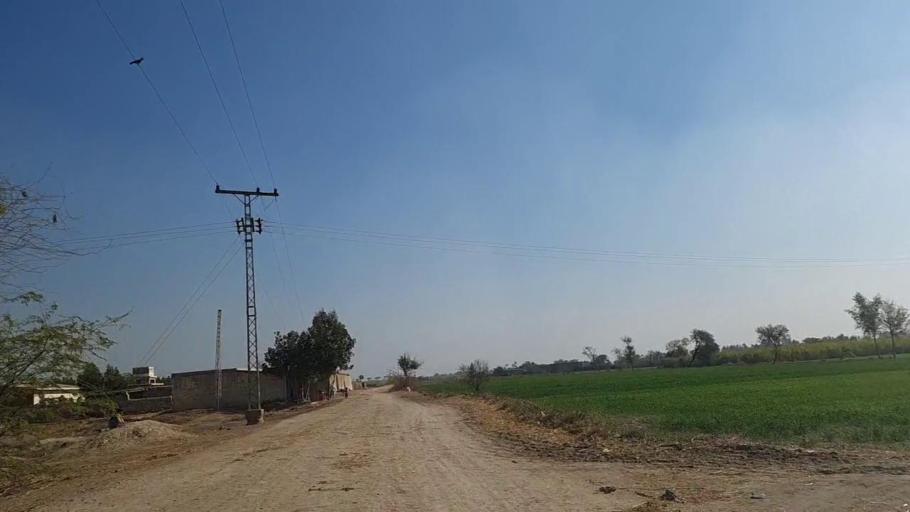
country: PK
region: Sindh
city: Daur
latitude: 26.4820
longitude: 68.3333
